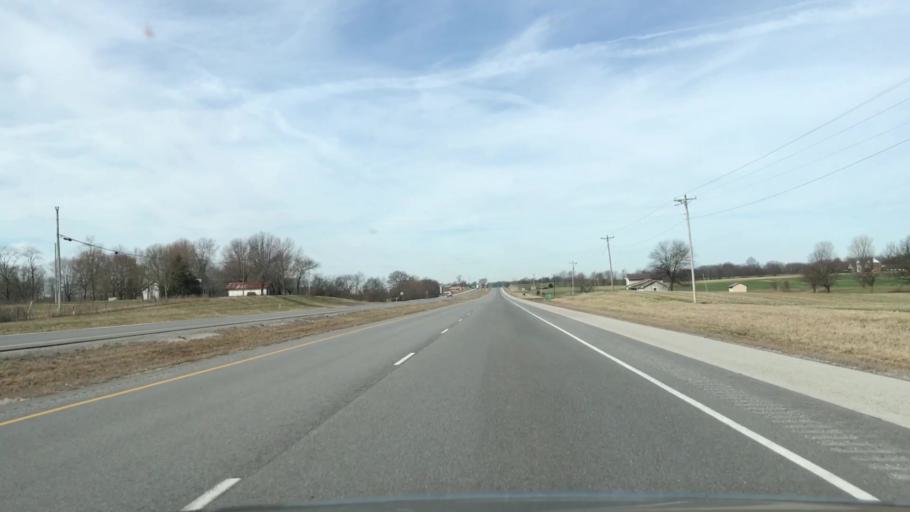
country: US
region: Kentucky
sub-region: Trigg County
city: Cadiz
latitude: 36.8820
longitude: -87.6903
